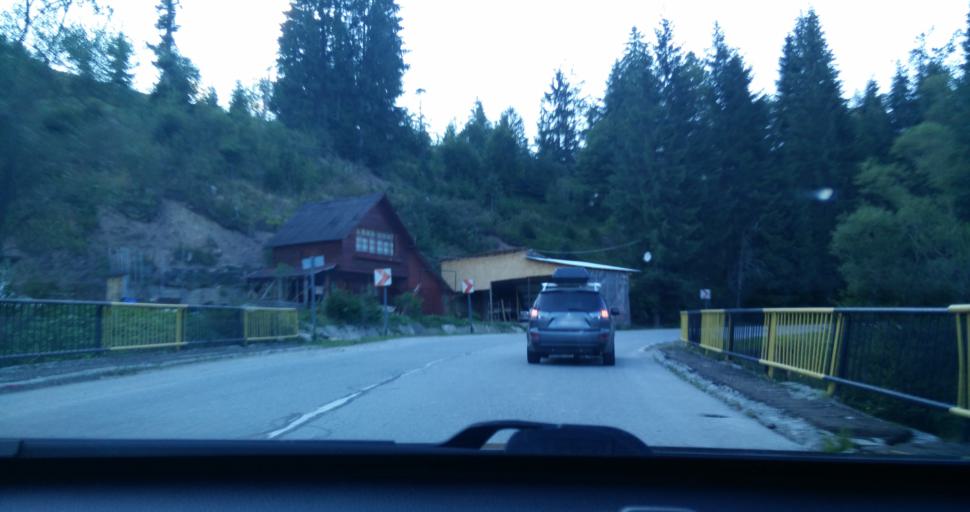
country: RO
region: Alba
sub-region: Comuna Arieseni
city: Arieseni
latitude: 46.4959
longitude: 22.7070
